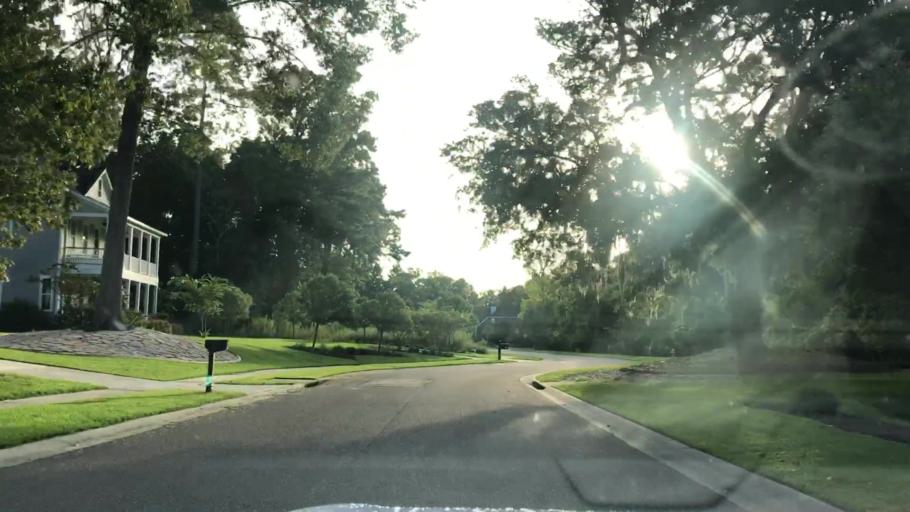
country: US
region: South Carolina
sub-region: Charleston County
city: Shell Point
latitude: 32.8392
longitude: -80.0772
